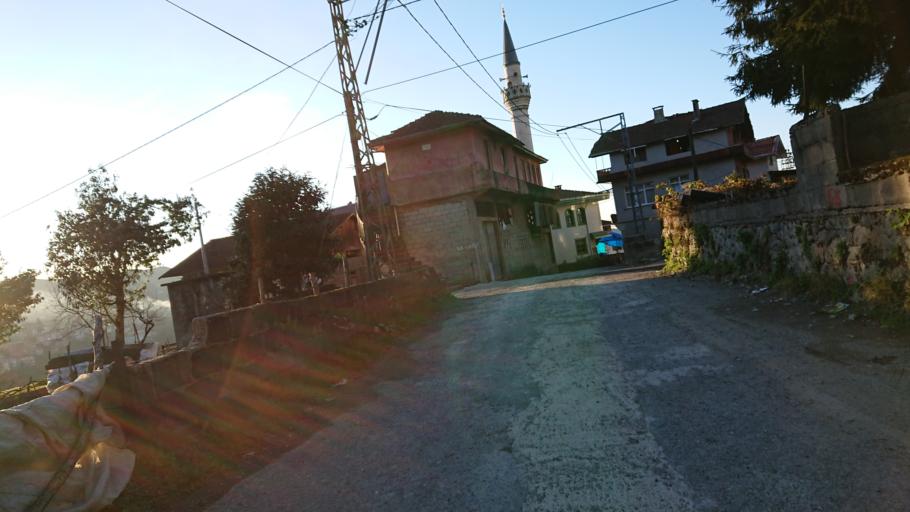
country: TR
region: Rize
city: Rize
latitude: 40.9825
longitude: 40.4944
